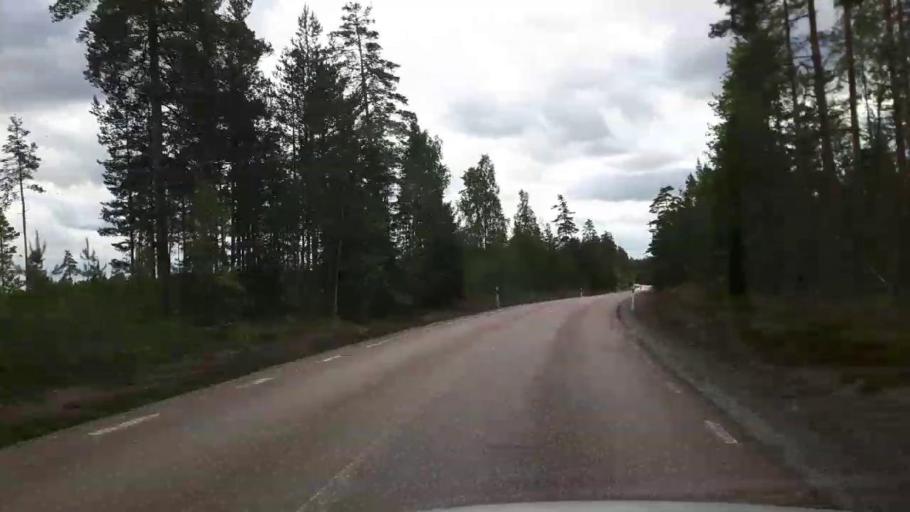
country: SE
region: Vaestmanland
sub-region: Fagersta Kommun
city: Fagersta
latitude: 59.8681
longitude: 15.8421
